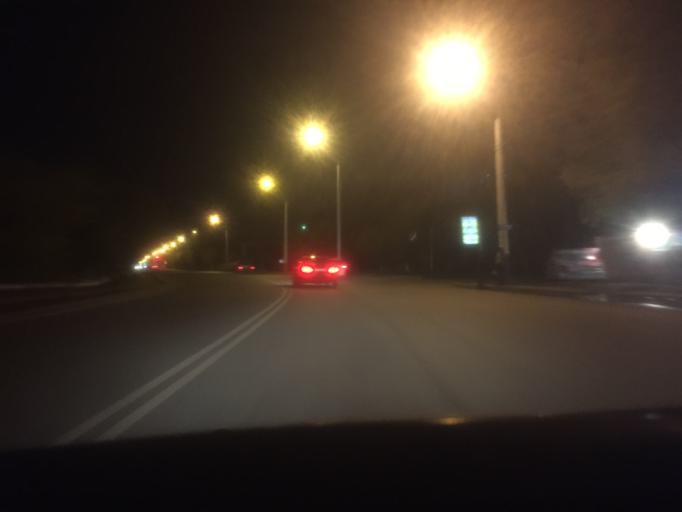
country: KZ
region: Astana Qalasy
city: Astana
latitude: 51.1948
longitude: 71.4044
